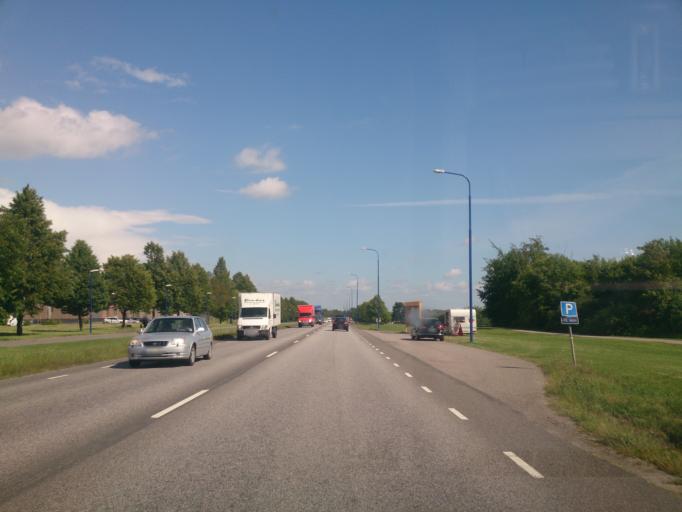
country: SE
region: OEstergoetland
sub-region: Norrkopings Kommun
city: Norrkoping
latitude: 58.6080
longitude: 16.1681
